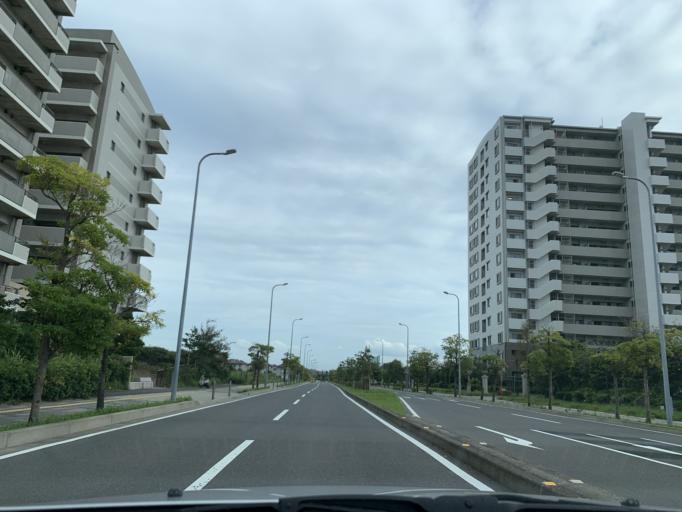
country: JP
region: Tokyo
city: Urayasu
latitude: 35.6441
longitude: 139.9289
